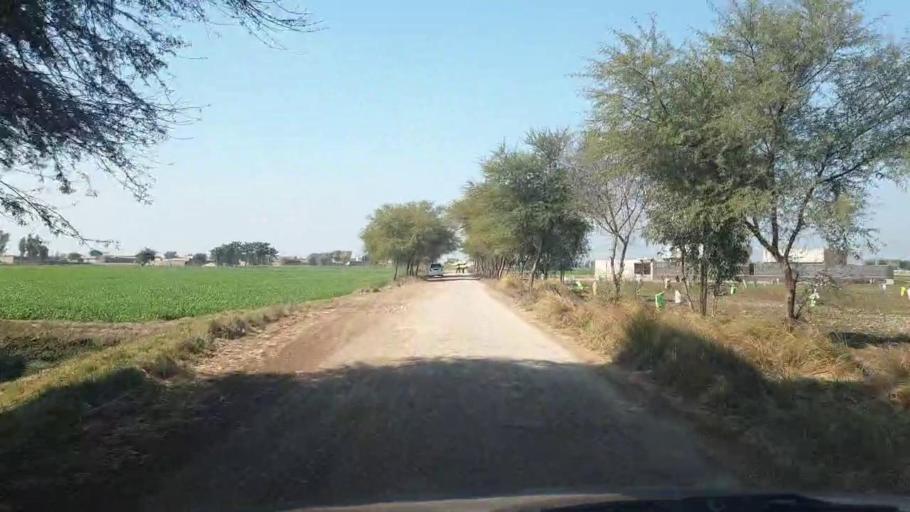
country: PK
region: Sindh
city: Bhit Shah
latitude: 25.8866
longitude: 68.5311
